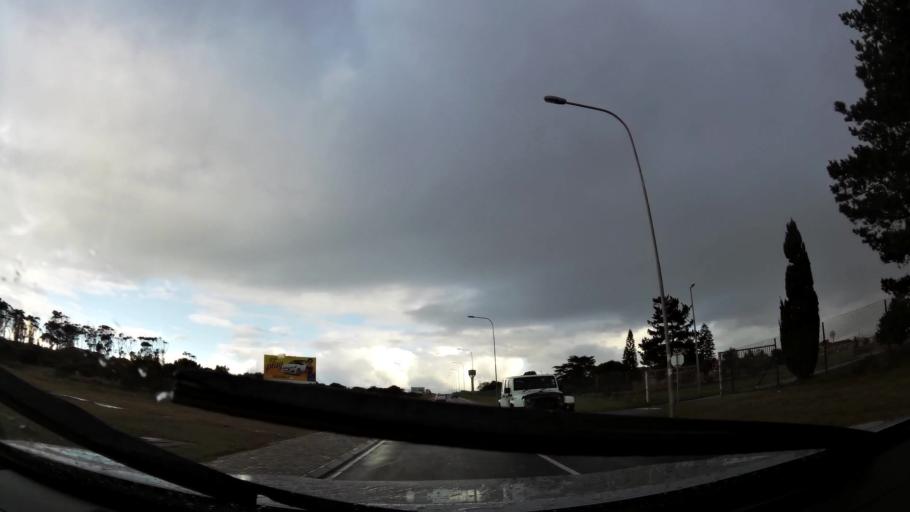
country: ZA
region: Western Cape
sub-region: Eden District Municipality
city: Mossel Bay
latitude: -34.1858
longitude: 22.0927
